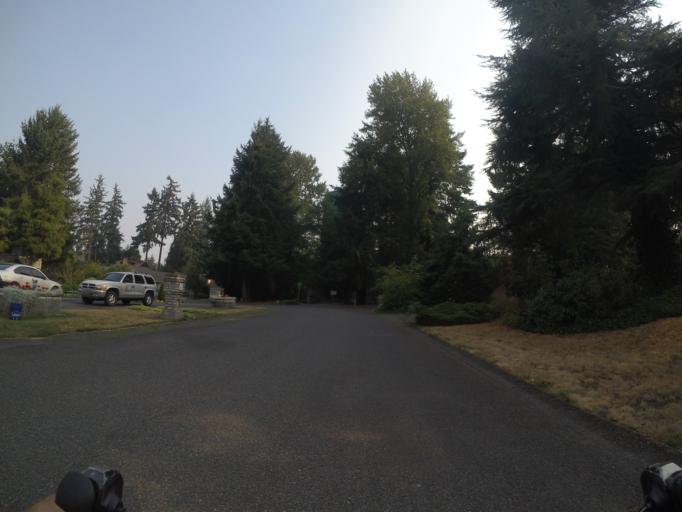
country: US
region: Washington
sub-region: Pierce County
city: Lakewood
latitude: 47.1421
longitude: -122.5233
